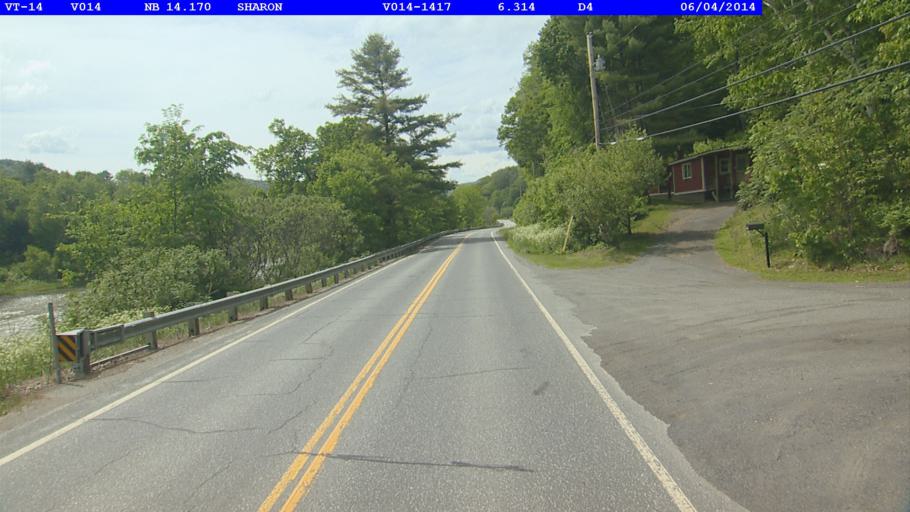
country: US
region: Vermont
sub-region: Windsor County
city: Woodstock
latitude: 43.7851
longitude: -72.4764
